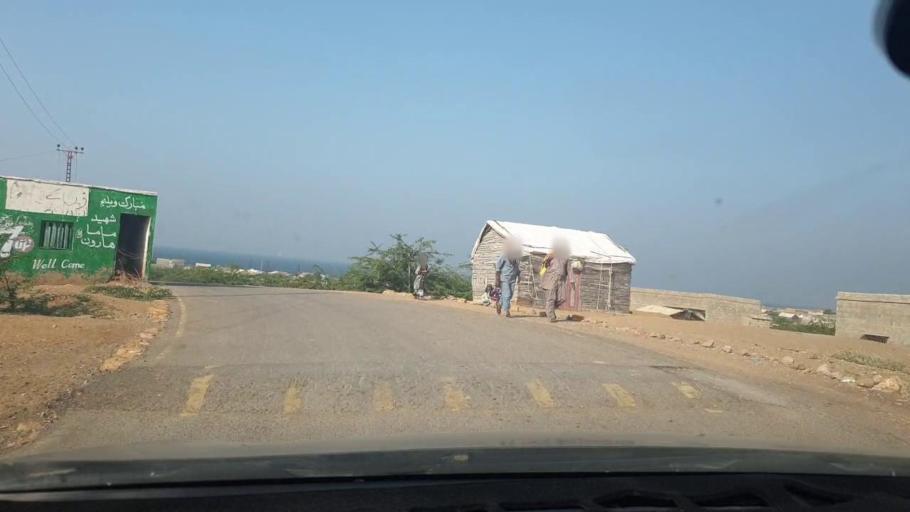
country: PK
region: Balochistan
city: Gadani
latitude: 24.8491
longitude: 66.6634
